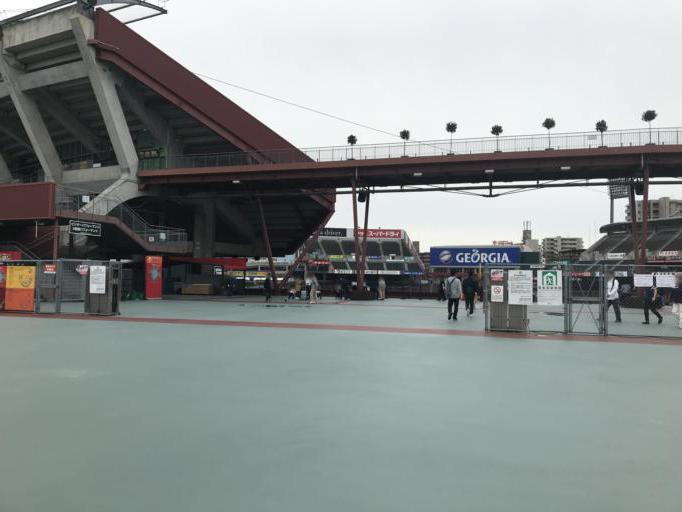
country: JP
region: Hiroshima
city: Hiroshima-shi
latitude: 34.3928
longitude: 132.4839
